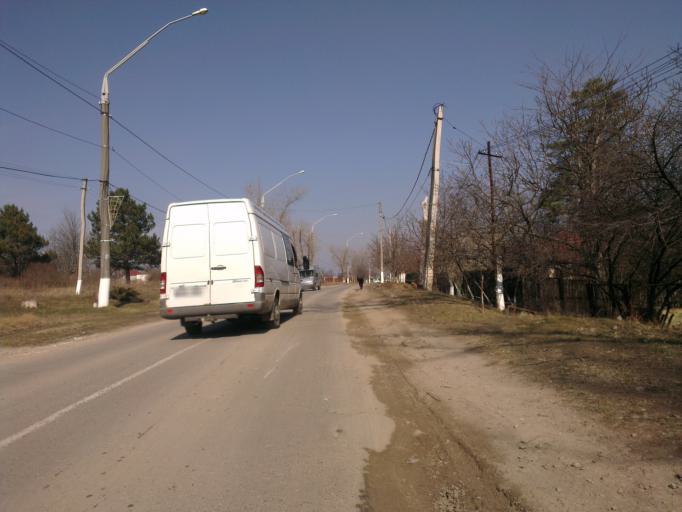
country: MD
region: Chisinau
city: Cricova
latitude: 47.1277
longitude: 28.8646
